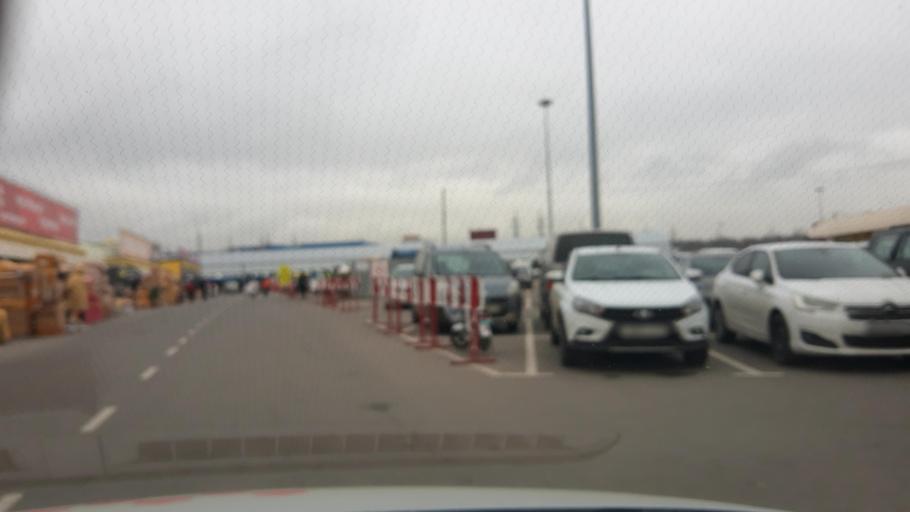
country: RU
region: Moscow
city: Lyublino
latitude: 55.6759
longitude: 37.7784
